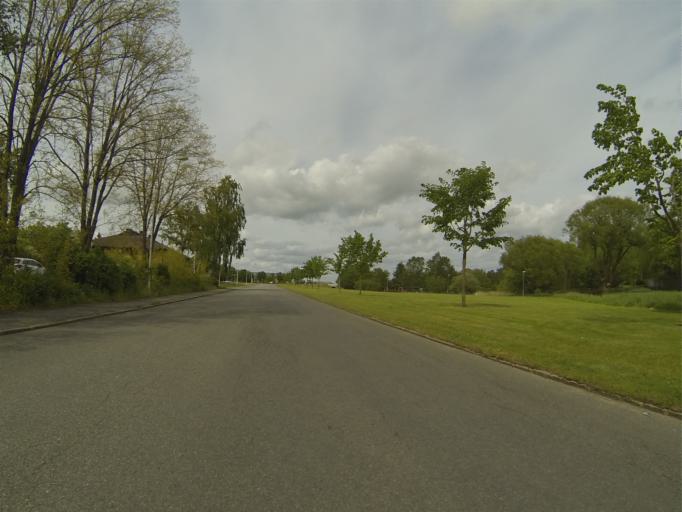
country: SE
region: Skane
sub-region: Tomelilla Kommun
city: Tomelilla
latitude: 55.5459
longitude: 13.9566
